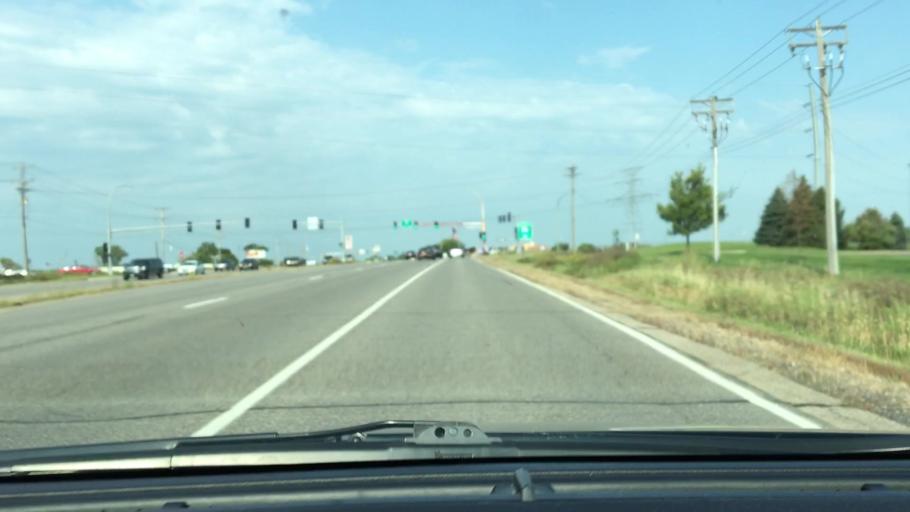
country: US
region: Minnesota
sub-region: Hennepin County
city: Plymouth
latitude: 45.0099
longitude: -93.4542
